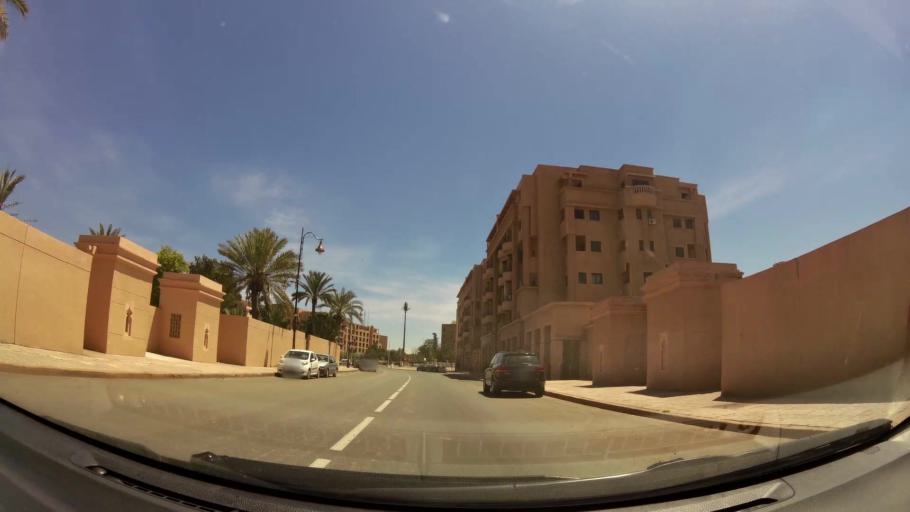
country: MA
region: Marrakech-Tensift-Al Haouz
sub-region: Marrakech
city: Marrakesh
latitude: 31.6242
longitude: -8.0161
